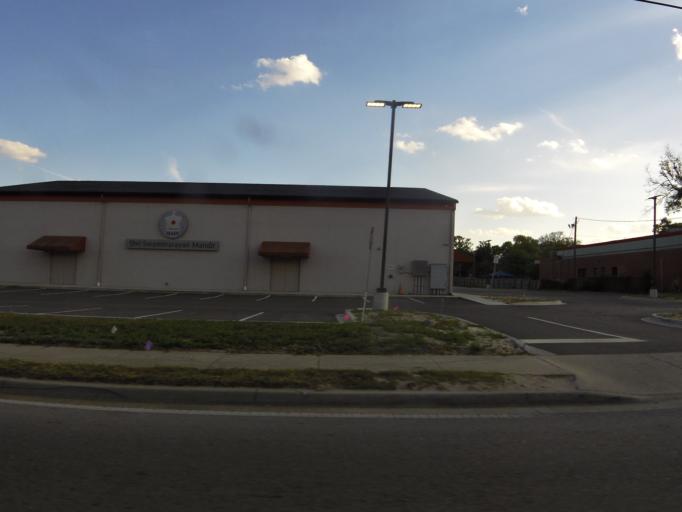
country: US
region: Florida
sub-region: Duval County
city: Jacksonville
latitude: 30.3521
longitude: -81.5720
